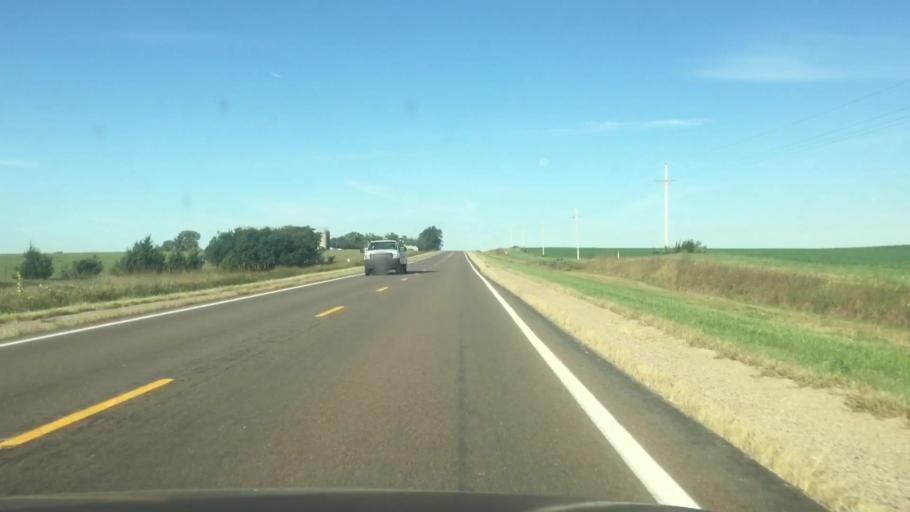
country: US
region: Nebraska
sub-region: Jefferson County
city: Fairbury
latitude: 40.1472
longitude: -97.3614
